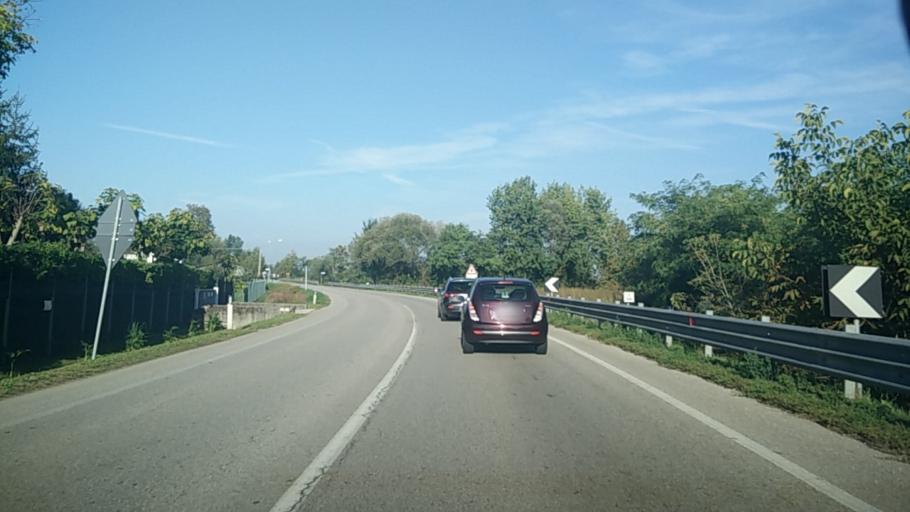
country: IT
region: Veneto
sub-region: Provincia di Padova
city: Piombino Dese
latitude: 45.6141
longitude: 12.0041
